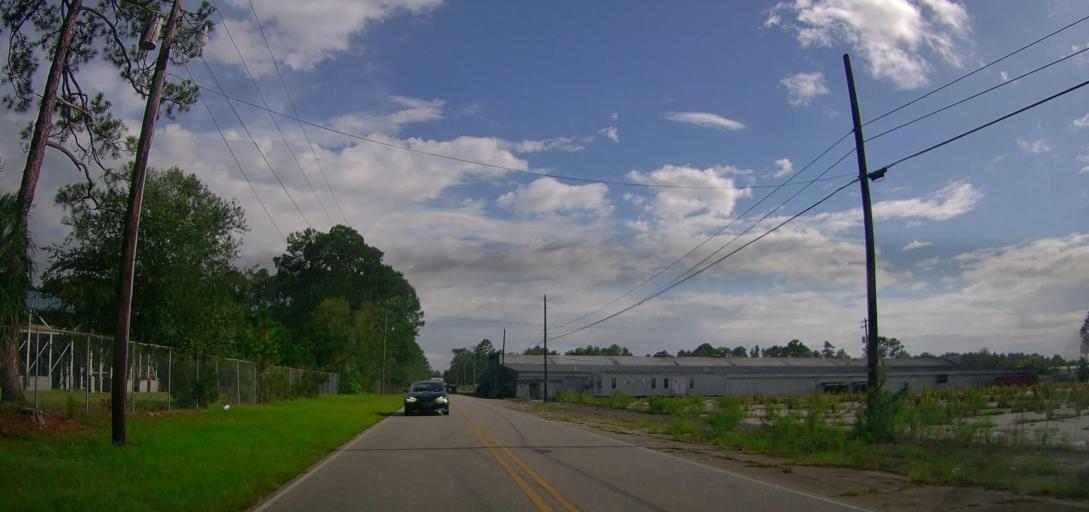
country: US
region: Georgia
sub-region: Coffee County
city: Douglas
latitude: 31.4934
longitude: -82.8589
